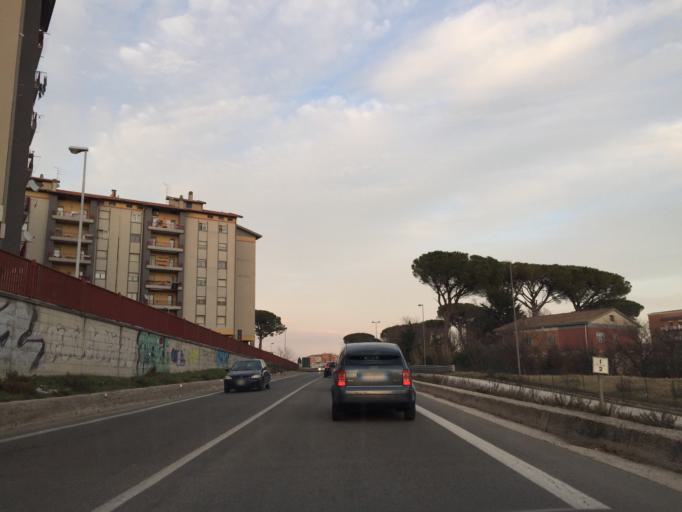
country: IT
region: Molise
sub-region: Provincia di Campobasso
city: Campobasso
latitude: 41.5568
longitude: 14.6721
